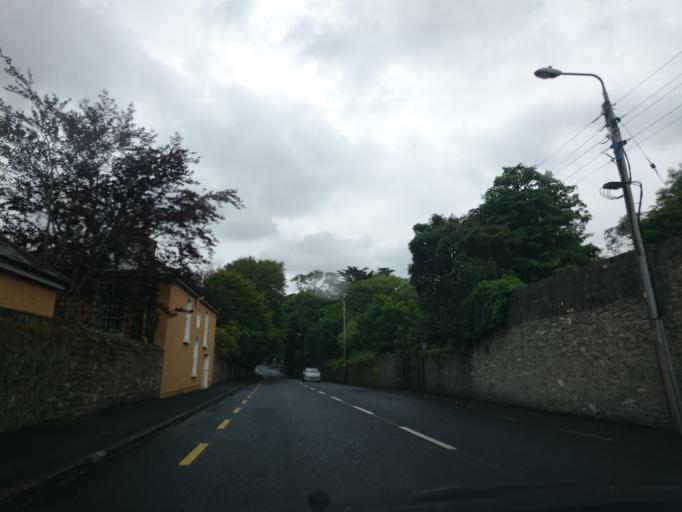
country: IE
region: Connaught
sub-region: Maigh Eo
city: Ballina
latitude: 54.2110
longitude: -9.2186
